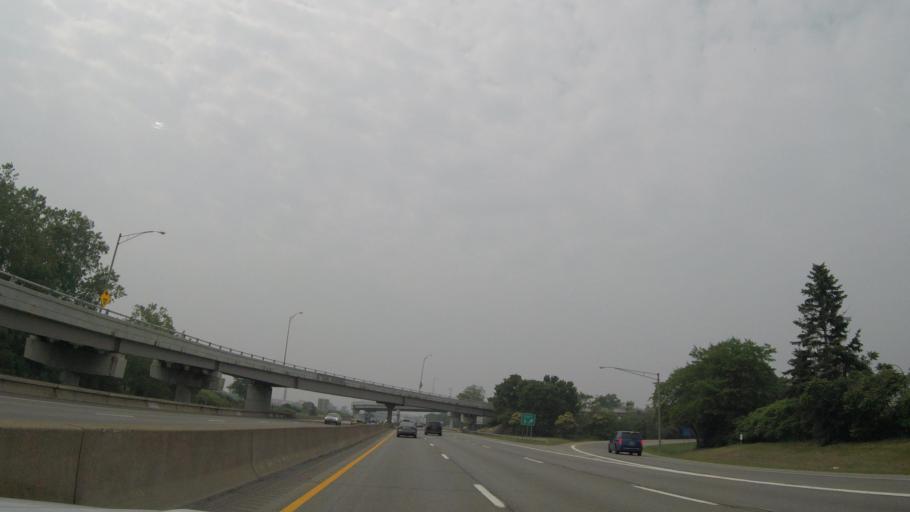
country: US
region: New York
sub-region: Erie County
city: Buffalo
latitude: 42.8887
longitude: -78.8882
